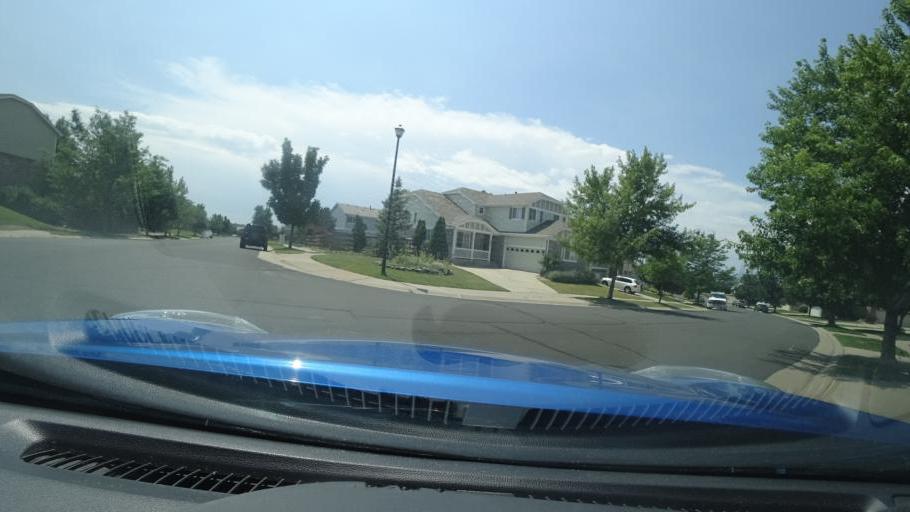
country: US
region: Colorado
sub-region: Adams County
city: Aurora
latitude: 39.6761
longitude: -104.7694
